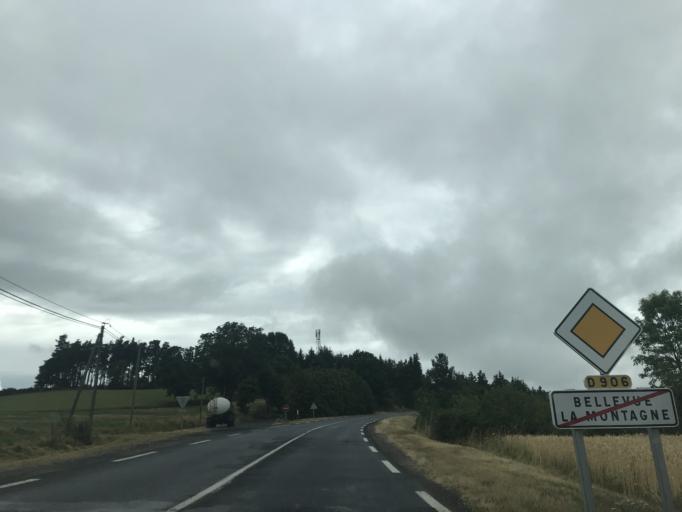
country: FR
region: Auvergne
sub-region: Departement de la Haute-Loire
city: Saint-Paulien
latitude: 45.2211
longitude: 3.8152
